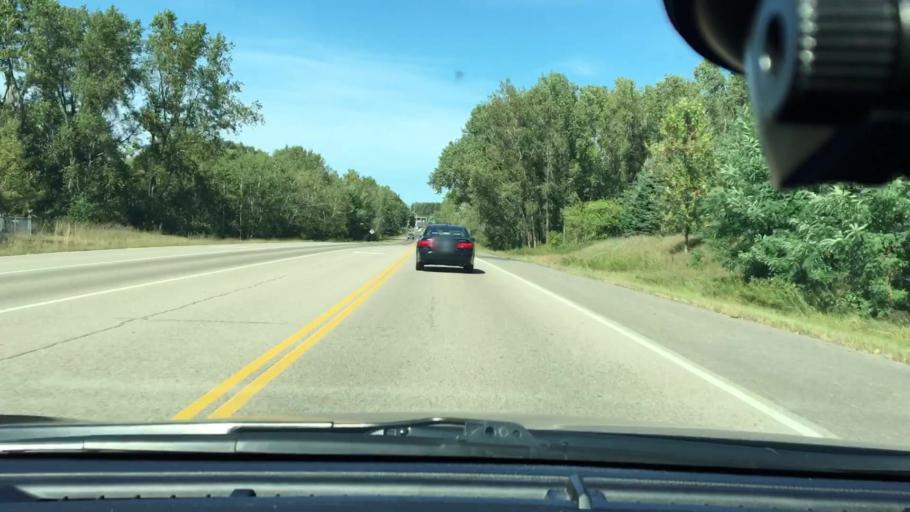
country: US
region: Minnesota
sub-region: Washington County
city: Mahtomedi
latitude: 45.0511
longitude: -92.9475
